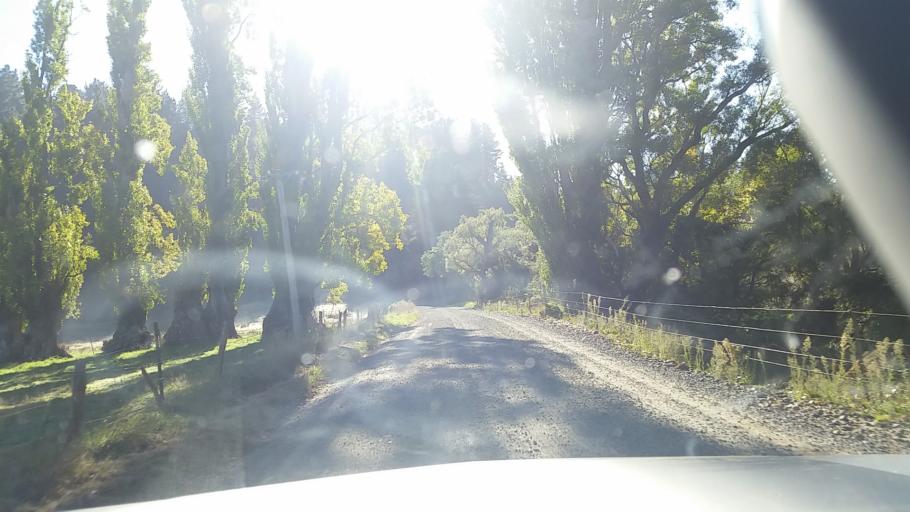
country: NZ
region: Marlborough
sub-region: Marlborough District
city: Blenheim
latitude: -41.4476
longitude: 173.8784
